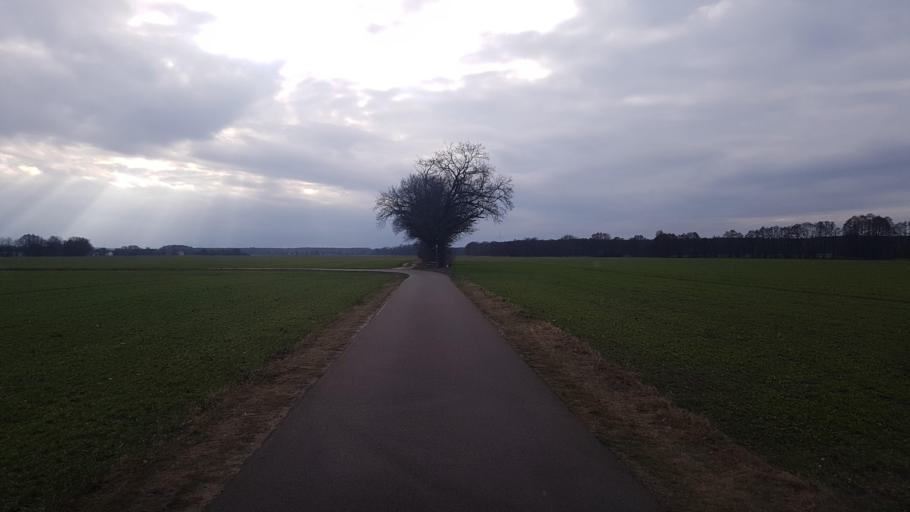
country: DE
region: Brandenburg
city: Golssen
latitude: 51.9532
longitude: 13.6086
